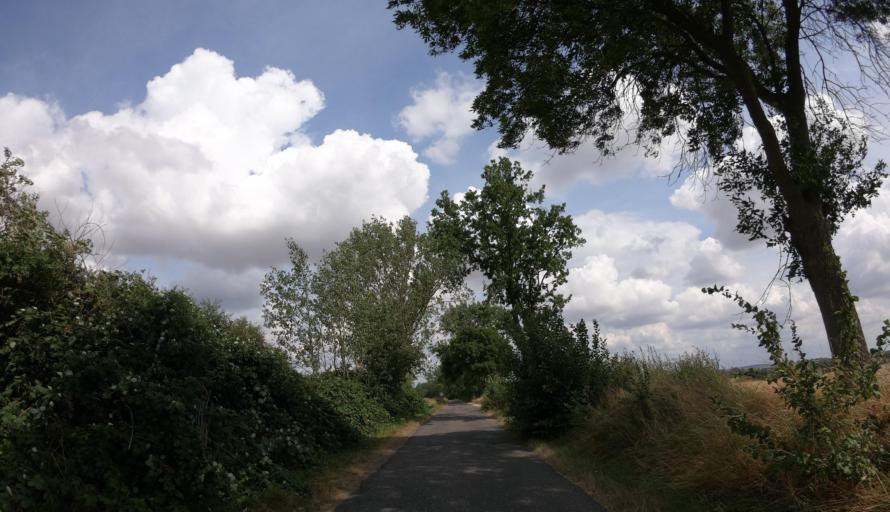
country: PL
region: West Pomeranian Voivodeship
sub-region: Powiat pyrzycki
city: Kozielice
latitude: 53.0618
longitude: 14.8927
